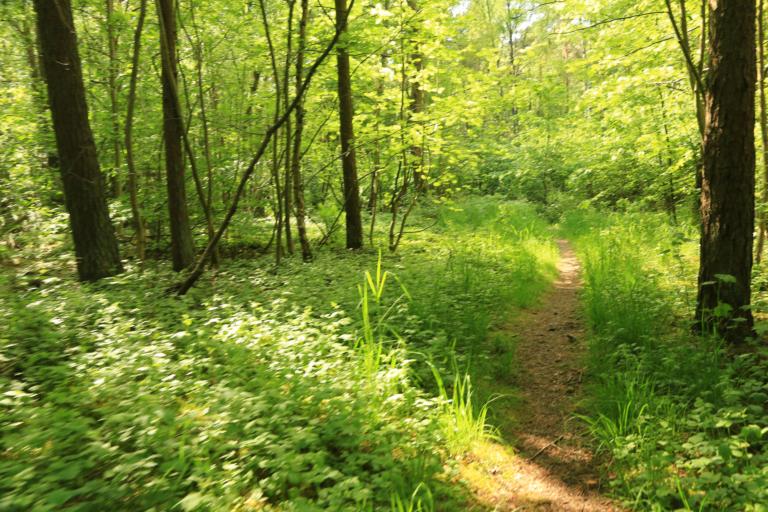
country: SE
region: Halland
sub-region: Varbergs Kommun
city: Varberg
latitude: 57.1080
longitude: 12.2878
